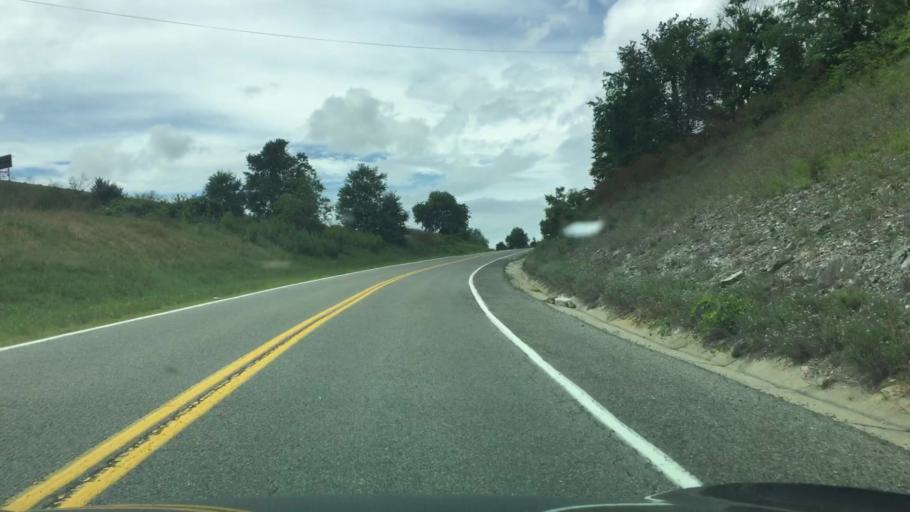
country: US
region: Virginia
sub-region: Wythe County
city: Wytheville
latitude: 36.9492
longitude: -80.9205
